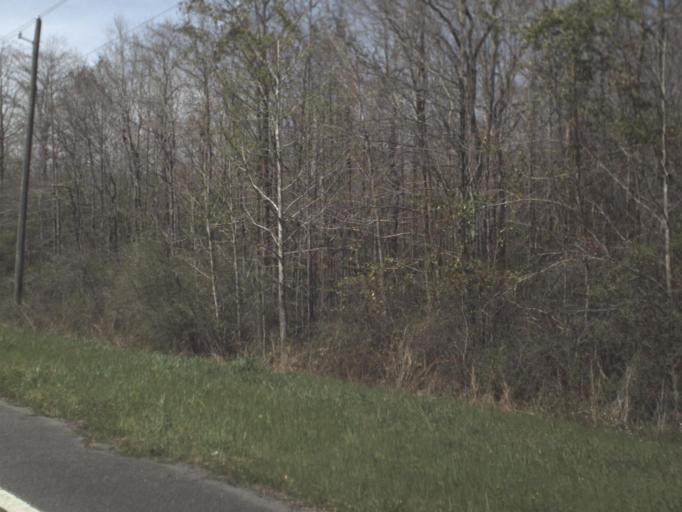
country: US
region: Florida
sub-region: Walton County
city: DeFuniak Springs
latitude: 30.7414
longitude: -85.9041
